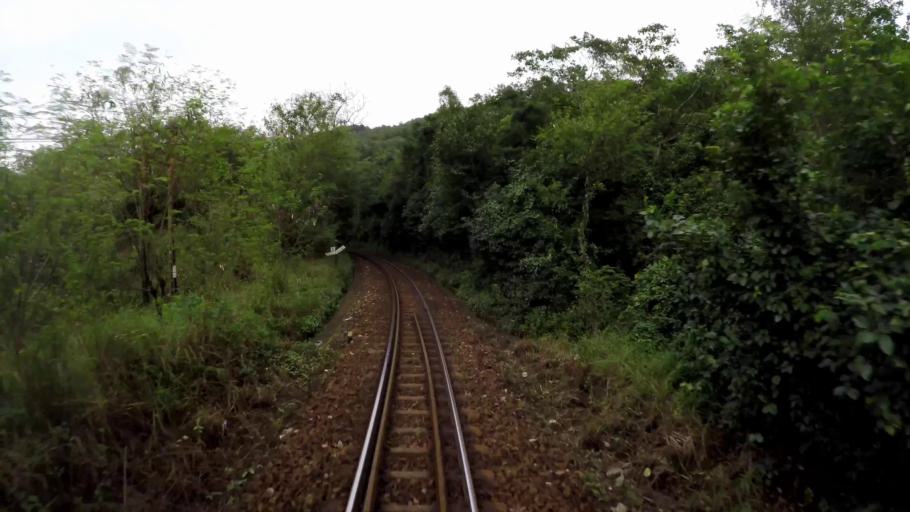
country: VN
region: Da Nang
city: Lien Chieu
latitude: 16.2066
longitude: 108.1217
